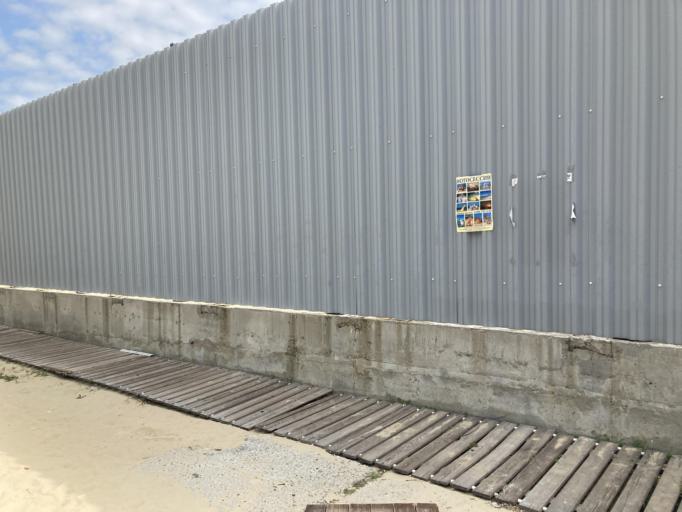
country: RU
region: Krasnodarskiy
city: Anapa
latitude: 44.9393
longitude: 37.3052
